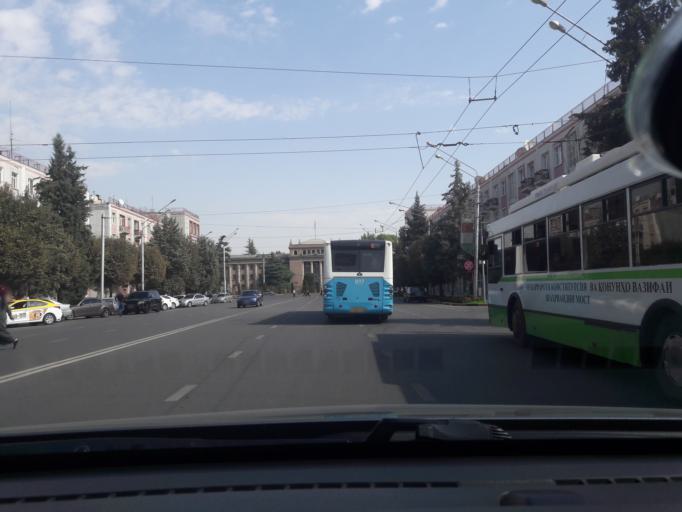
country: TJ
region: Dushanbe
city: Dushanbe
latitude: 38.5830
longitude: 68.7849
